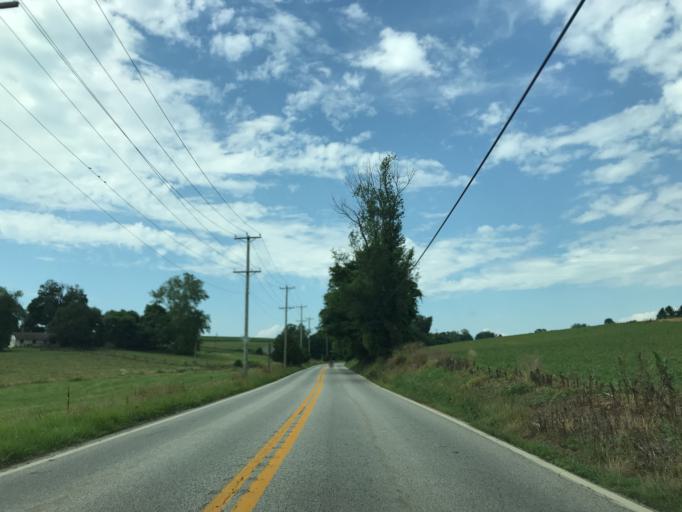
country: US
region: Maryland
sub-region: Harford County
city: Jarrettsville
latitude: 39.6582
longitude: -76.4075
